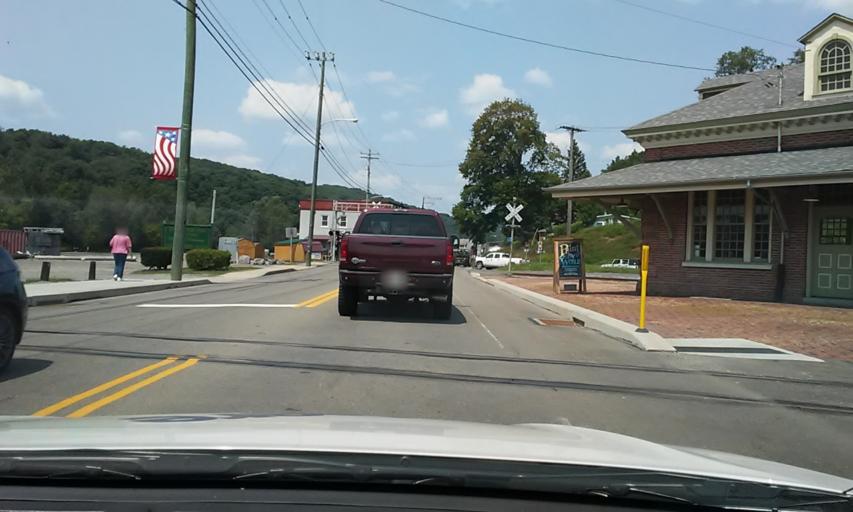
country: US
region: Pennsylvania
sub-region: Elk County
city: Ridgway
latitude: 41.4250
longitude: -78.7315
